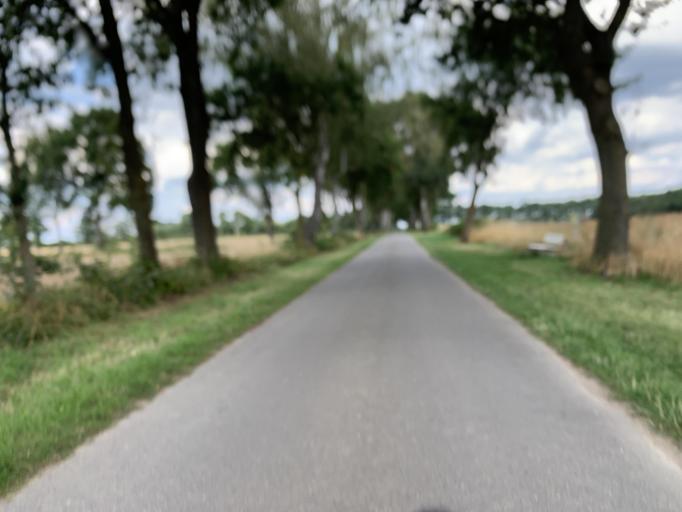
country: DE
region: Lower Saxony
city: Reinstorf
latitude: 53.2221
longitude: 10.5977
